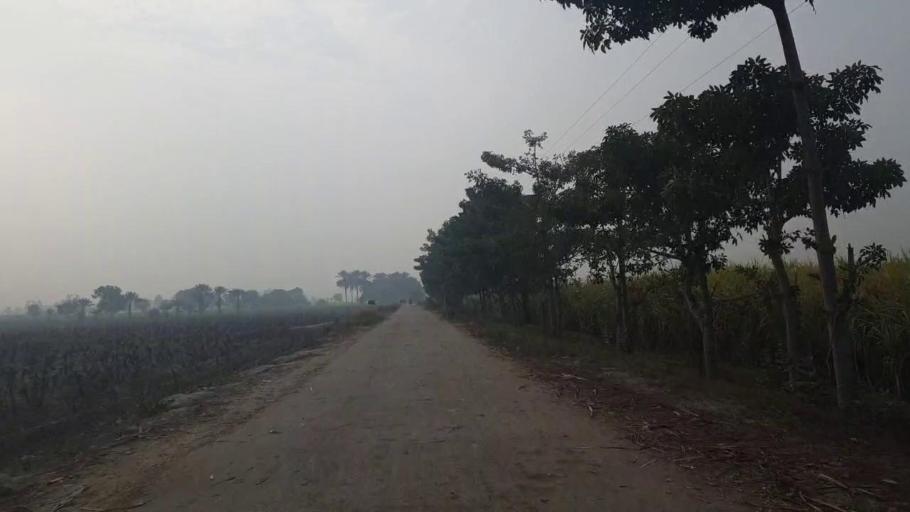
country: PK
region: Sindh
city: Tando Adam
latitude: 25.7177
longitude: 68.6804
